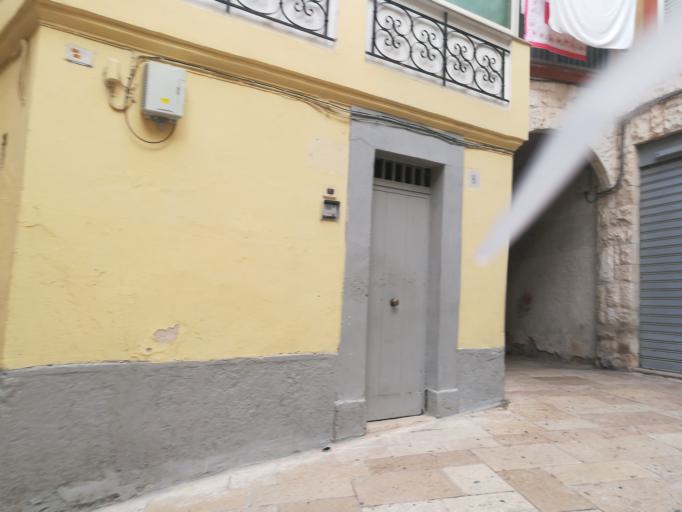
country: IT
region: Apulia
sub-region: Provincia di Bari
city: Bari
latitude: 41.1309
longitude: 16.8691
